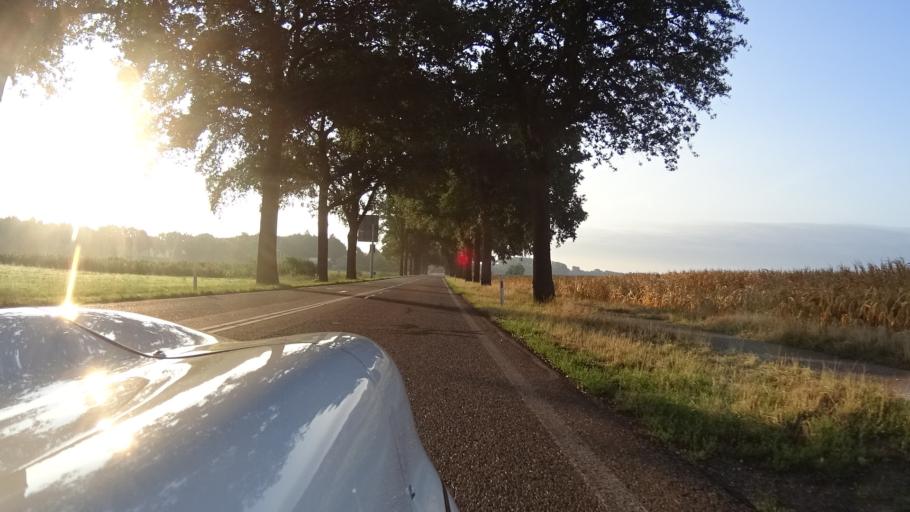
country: NL
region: Limburg
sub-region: Gemeente Bergen
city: Wellerlooi
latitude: 51.5543
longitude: 6.1016
